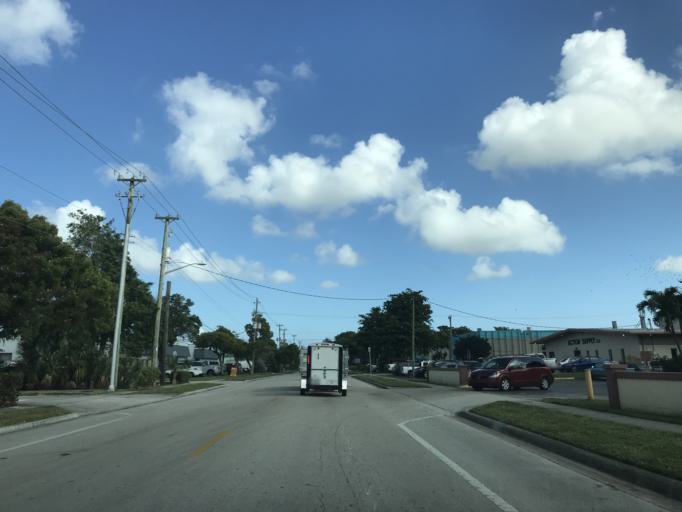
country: US
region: Florida
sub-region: Broward County
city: Margate
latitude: 26.2486
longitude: -80.1982
